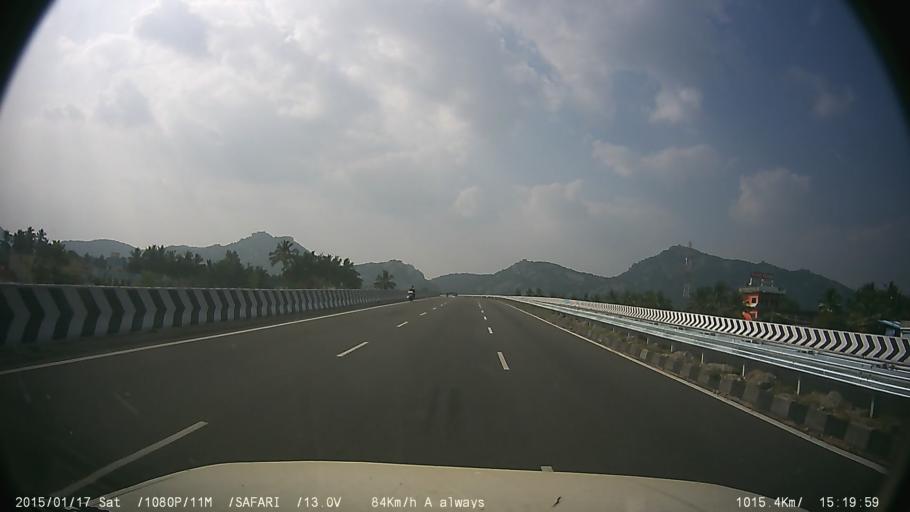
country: IN
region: Tamil Nadu
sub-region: Krishnagiri
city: Krishnagiri
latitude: 12.5997
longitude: 78.1320
